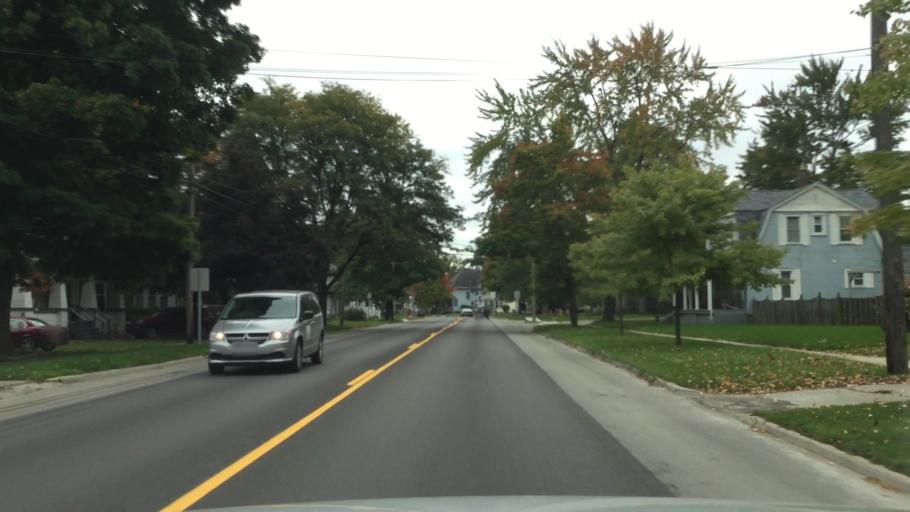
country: US
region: Michigan
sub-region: Macomb County
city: Richmond
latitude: 42.8162
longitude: -82.7596
